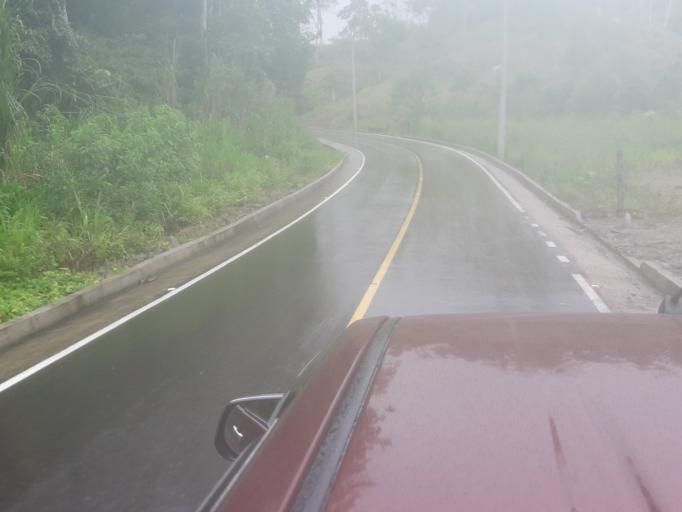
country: EC
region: Napo
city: Tena
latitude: -1.0230
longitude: -77.6629
